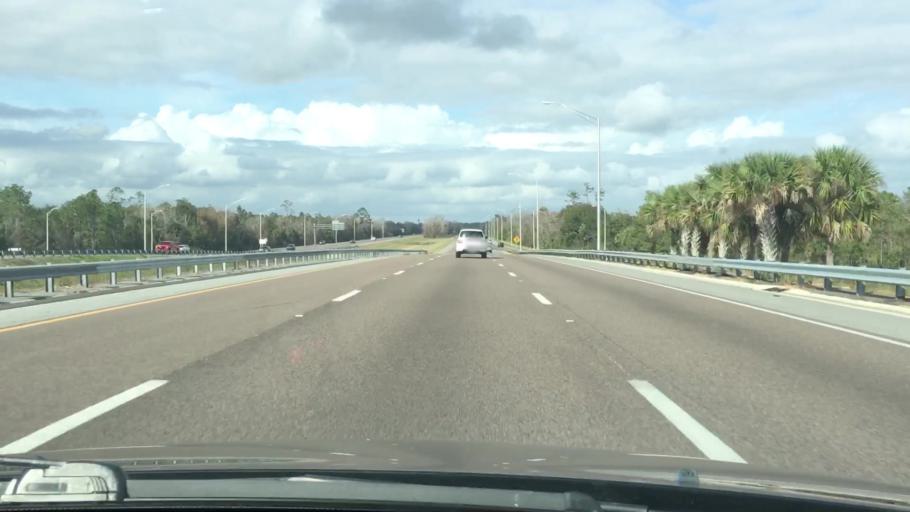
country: US
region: Florida
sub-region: Volusia County
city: Edgewater
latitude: 28.9517
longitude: -80.9508
